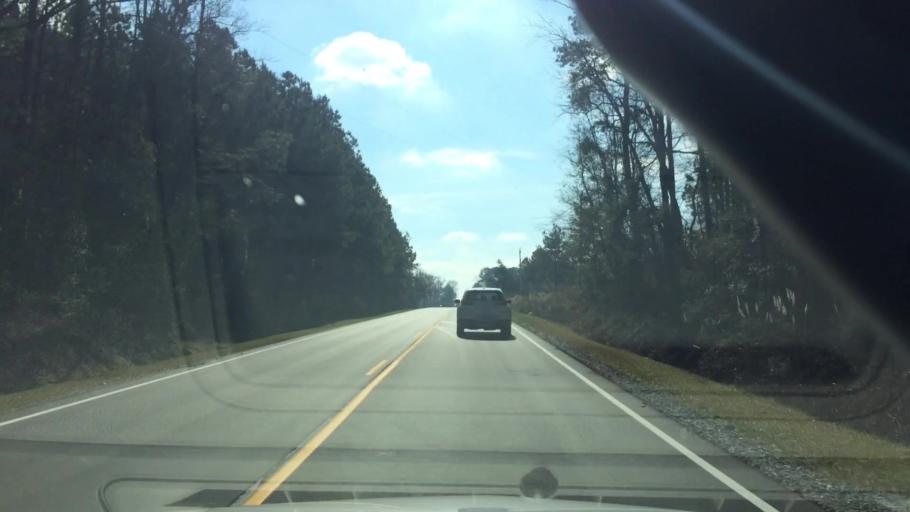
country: US
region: North Carolina
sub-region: Duplin County
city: Beulaville
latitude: 34.9394
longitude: -77.7698
